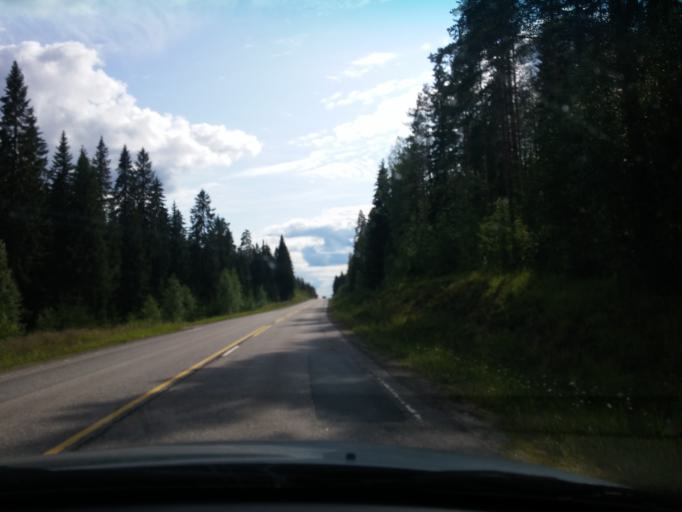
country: FI
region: Central Finland
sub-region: Keuruu
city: Keuruu
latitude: 62.3089
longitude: 24.7298
